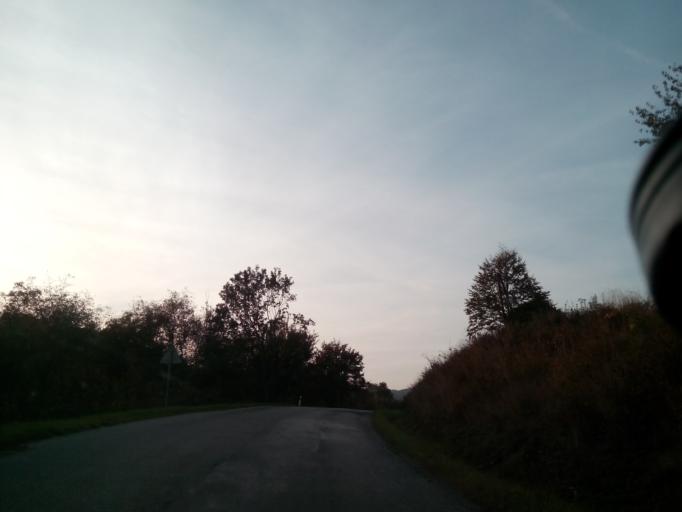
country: SK
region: Presovsky
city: Svidnik
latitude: 49.3563
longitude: 21.4449
